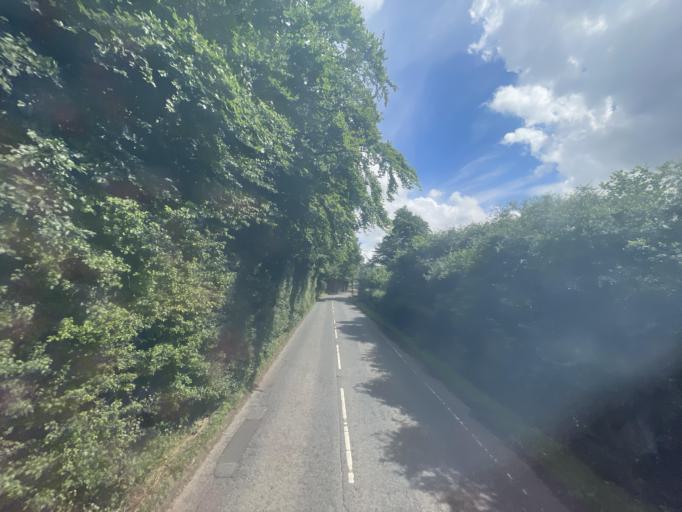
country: GB
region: England
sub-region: Kent
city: Westerham
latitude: 51.2913
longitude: 0.0570
